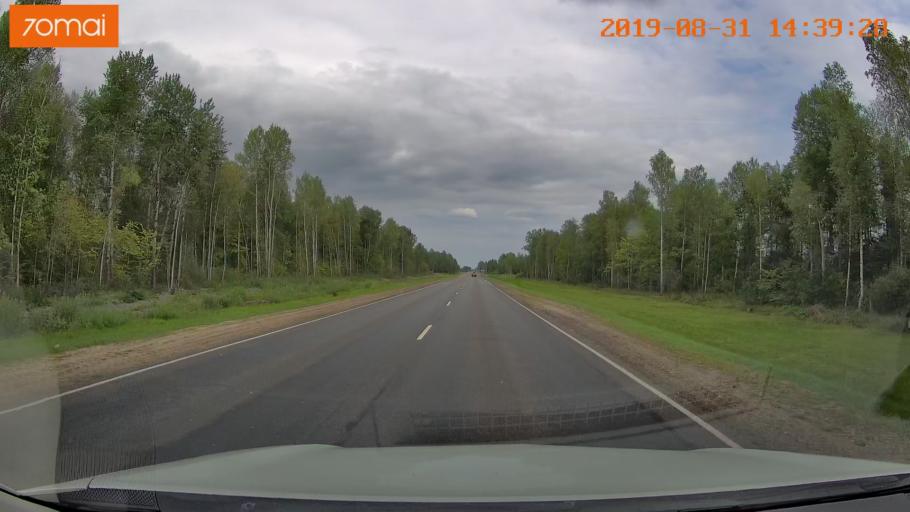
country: RU
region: Smolensk
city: Yekimovichi
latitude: 54.1918
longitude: 33.5533
